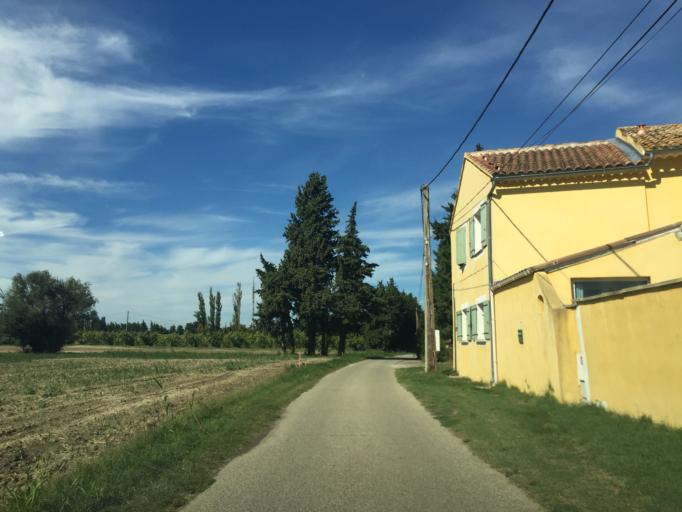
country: FR
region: Provence-Alpes-Cote d'Azur
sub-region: Departement du Vaucluse
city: Mornas
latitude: 44.1824
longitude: 4.7345
